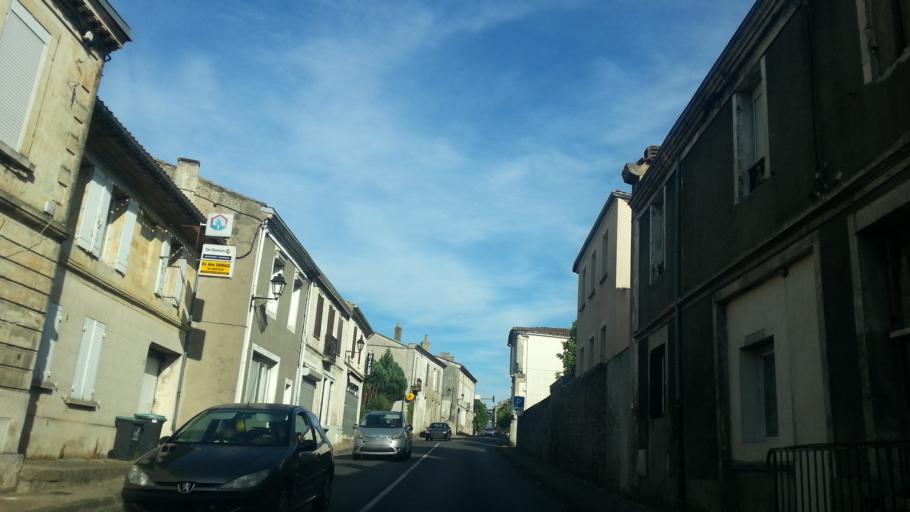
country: FR
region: Aquitaine
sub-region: Departement de la Gironde
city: Castres-Gironde
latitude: 44.6973
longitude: -0.4467
